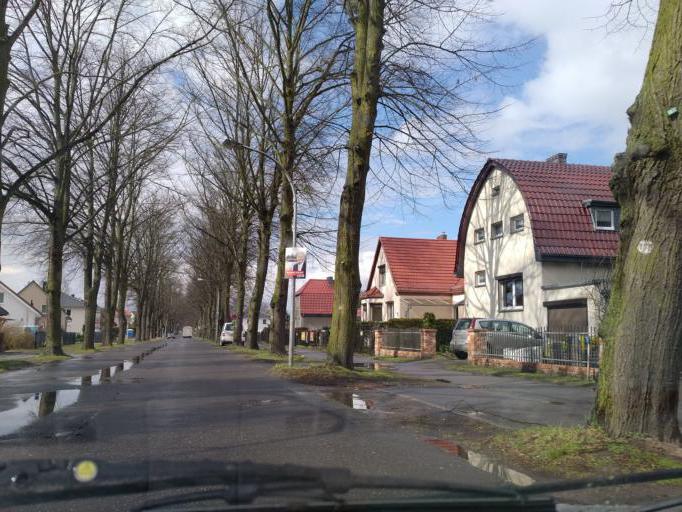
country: DE
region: Brandenburg
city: Falkensee
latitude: 52.5550
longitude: 13.1118
